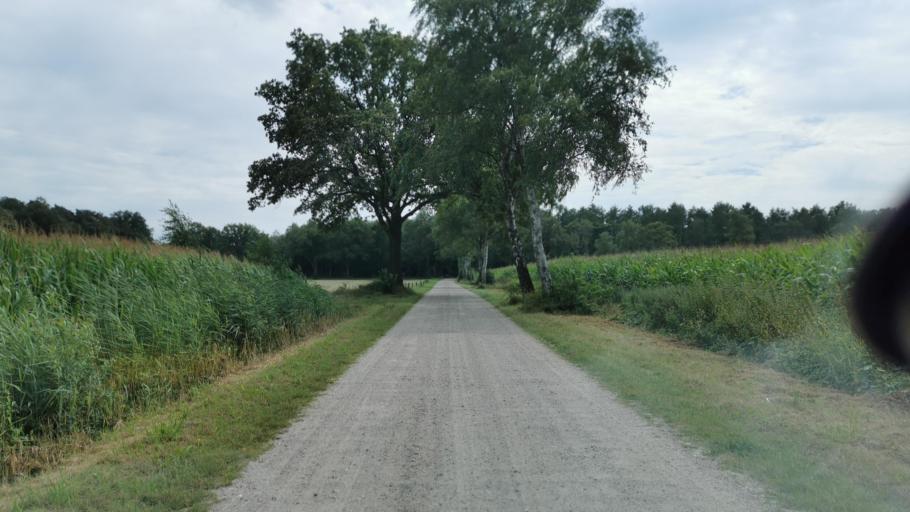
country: NL
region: Overijssel
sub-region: Gemeente Losser
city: Losser
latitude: 52.2510
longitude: 6.9567
